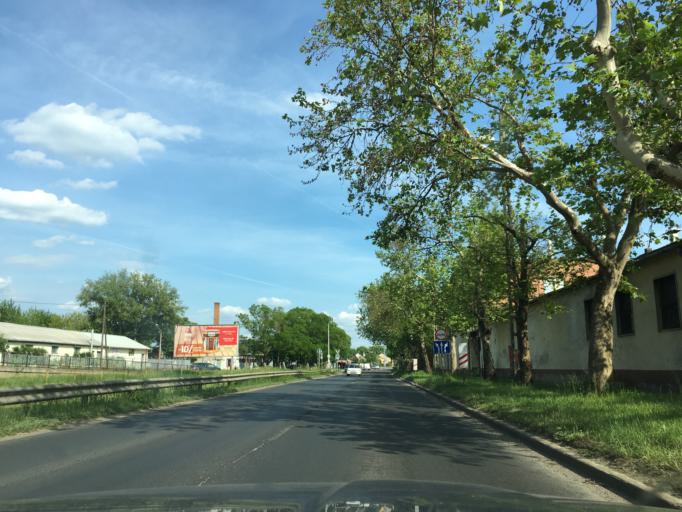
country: HU
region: Hajdu-Bihar
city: Debrecen
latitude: 47.5205
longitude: 21.6560
